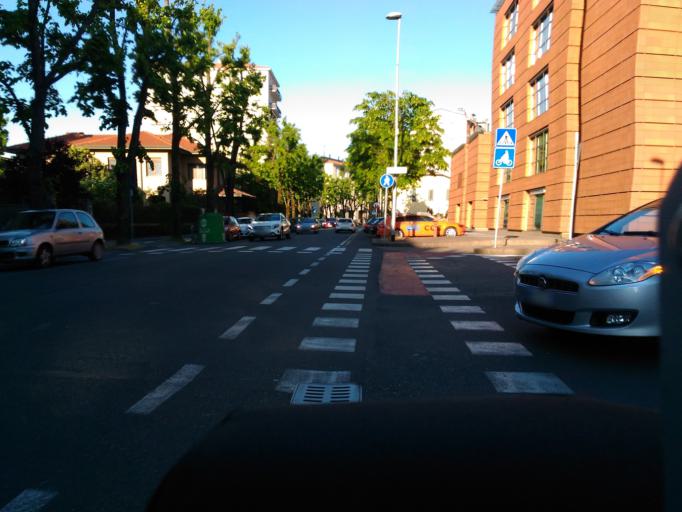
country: IT
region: Lombardy
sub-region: Provincia di Lodi
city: Lodi
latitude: 45.3120
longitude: 9.4951
